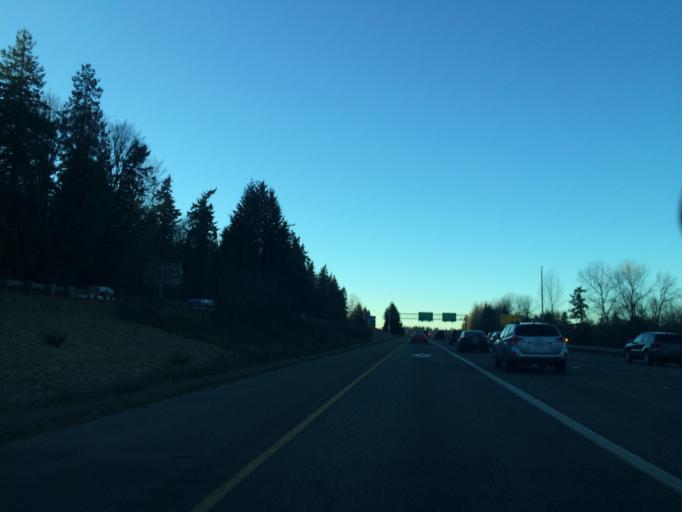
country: US
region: Washington
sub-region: King County
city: West Lake Sammamish
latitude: 47.5744
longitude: -122.1212
